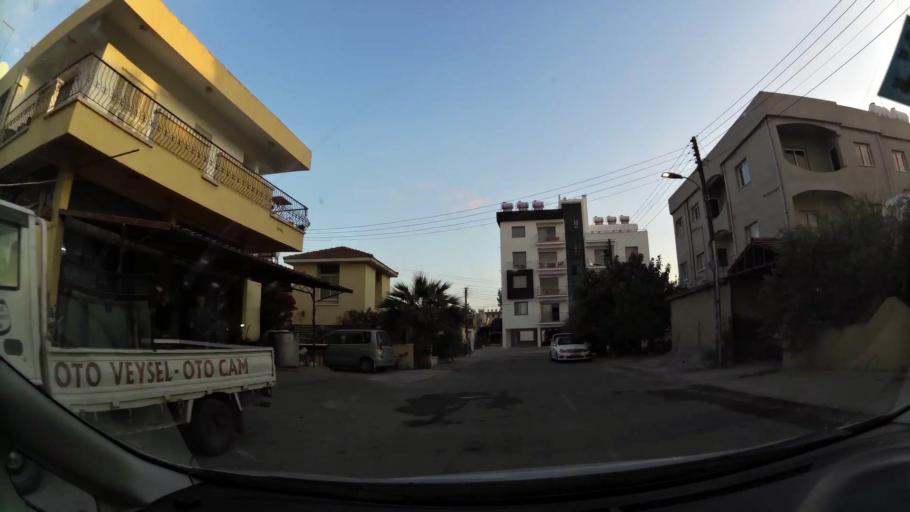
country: CY
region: Lefkosia
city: Nicosia
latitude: 35.2008
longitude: 33.3717
